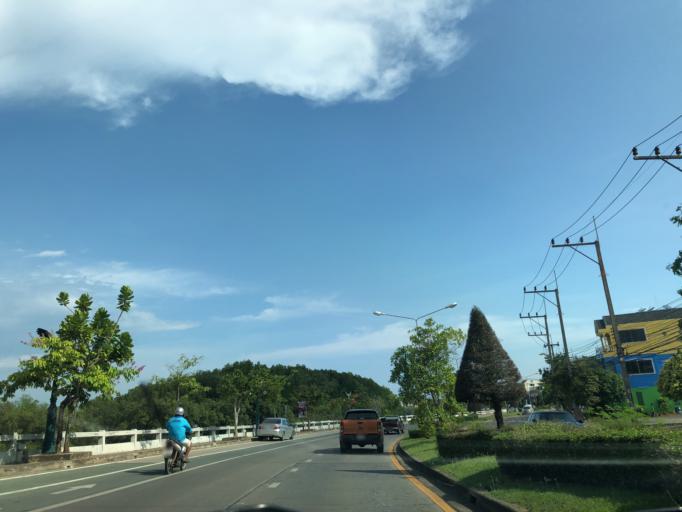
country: TH
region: Krabi
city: Krabi
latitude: 8.0741
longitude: 98.9170
